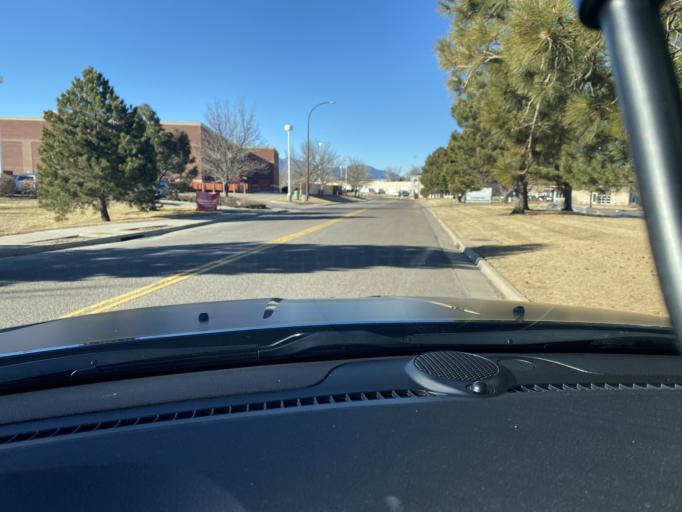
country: US
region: Colorado
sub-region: Jefferson County
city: Applewood
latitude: 39.8142
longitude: -105.1615
